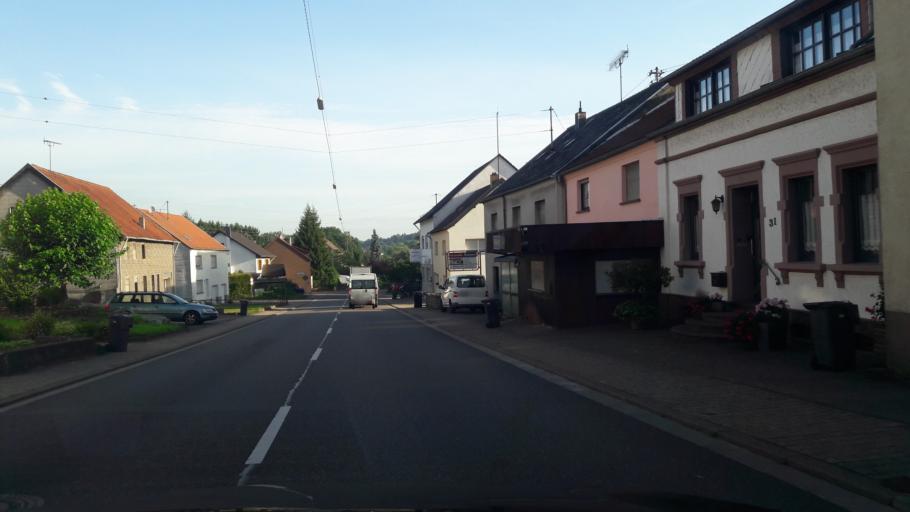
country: DE
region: Saarland
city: Lebach
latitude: 49.3913
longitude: 6.9235
